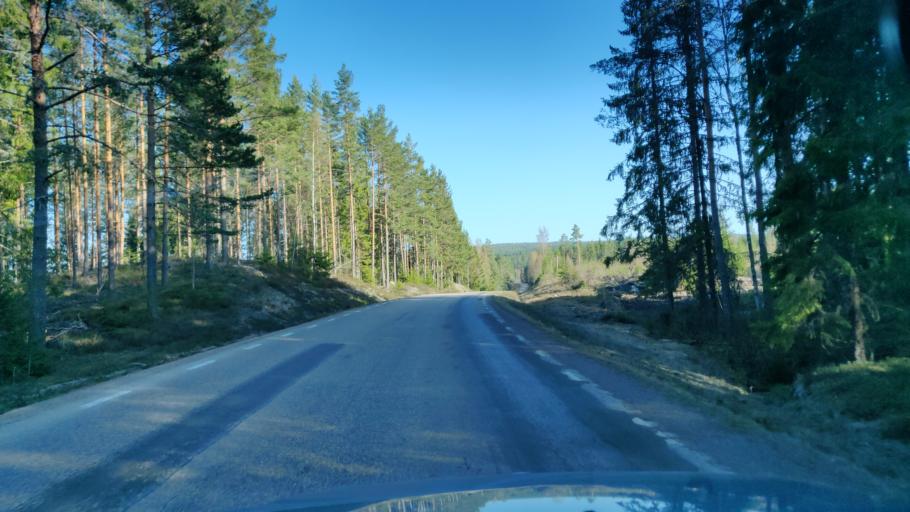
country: SE
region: Vaermland
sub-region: Sunne Kommun
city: Sunne
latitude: 59.9916
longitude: 13.3076
